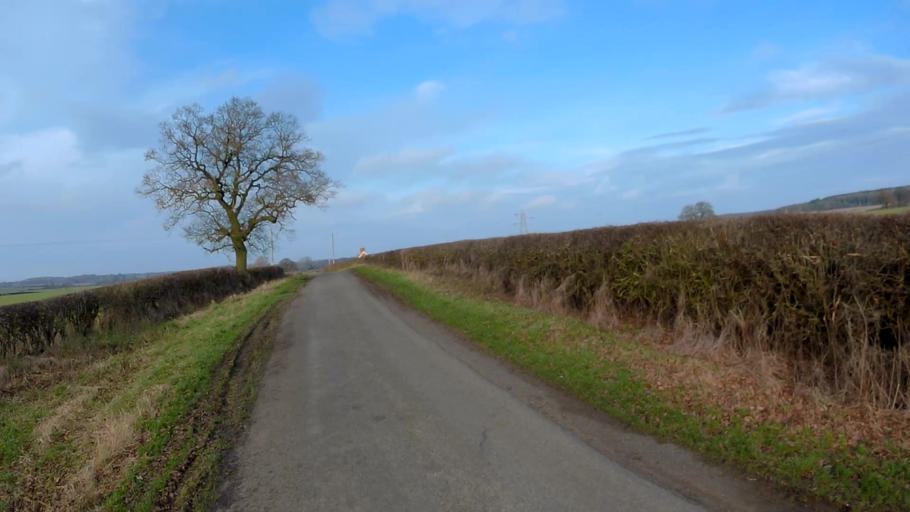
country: GB
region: England
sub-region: Lincolnshire
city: Bourne
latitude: 52.7663
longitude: -0.4214
